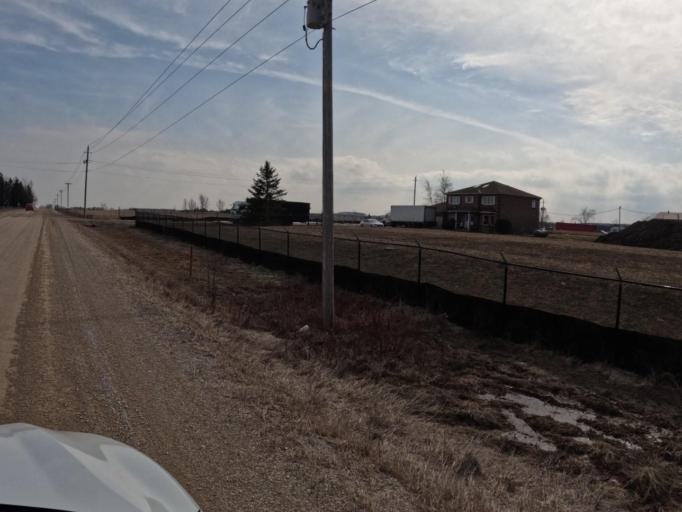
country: CA
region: Ontario
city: Orangeville
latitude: 43.8839
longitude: -80.2976
